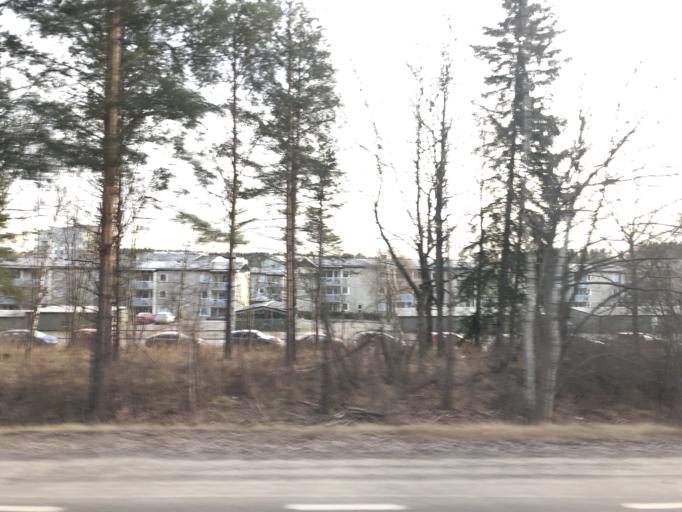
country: SE
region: Stockholm
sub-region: Jarfalla Kommun
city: Jakobsberg
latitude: 59.4112
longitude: 17.7966
